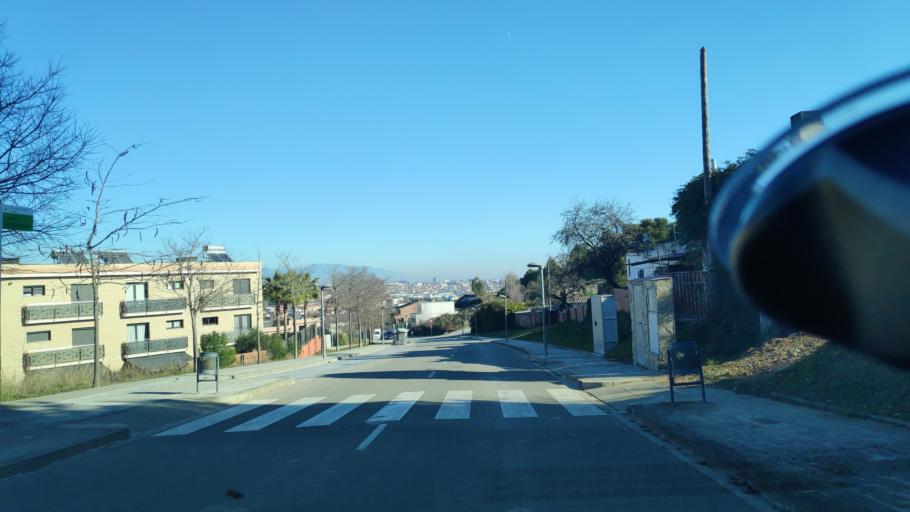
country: ES
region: Catalonia
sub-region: Provincia de Barcelona
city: Sant Quirze del Valles
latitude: 41.5239
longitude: 2.0754
